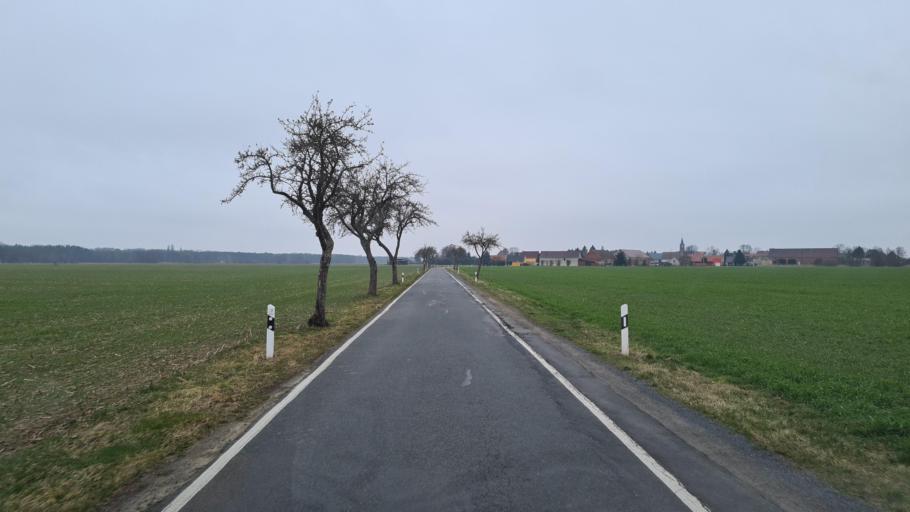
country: DE
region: Brandenburg
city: Herzberg
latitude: 51.6571
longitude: 13.1801
